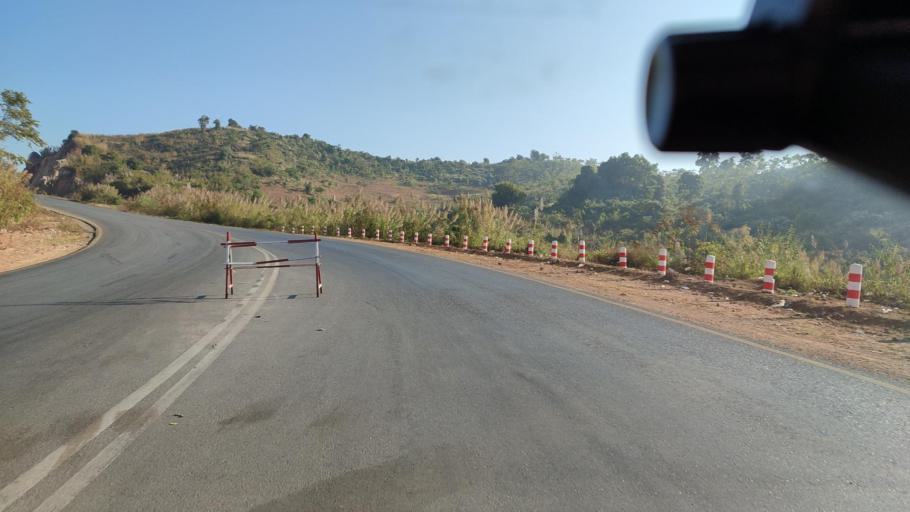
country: MM
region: Shan
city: Lashio
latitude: 23.0653
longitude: 97.7750
